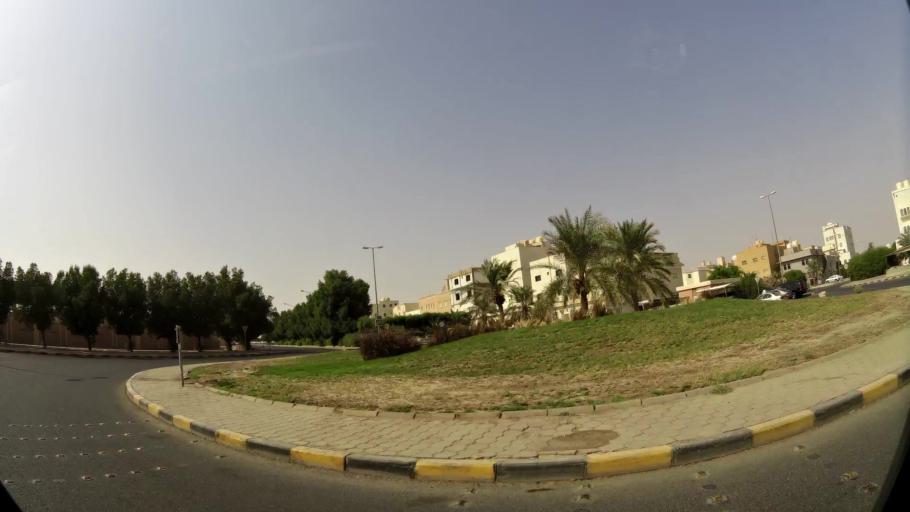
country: KW
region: Muhafazat al Jahra'
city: Al Jahra'
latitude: 29.3310
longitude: 47.6513
